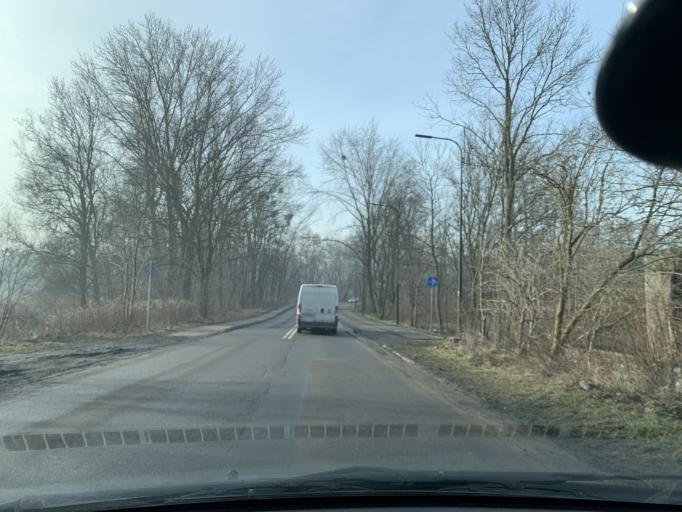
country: PL
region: Silesian Voivodeship
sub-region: Swietochlowice
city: Swietochlowice
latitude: 50.3284
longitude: 18.8625
